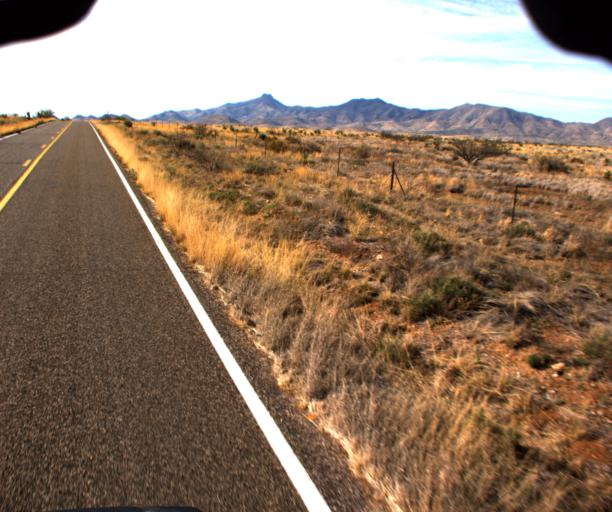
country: US
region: Arizona
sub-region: Cochise County
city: Willcox
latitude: 32.0976
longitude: -109.5386
